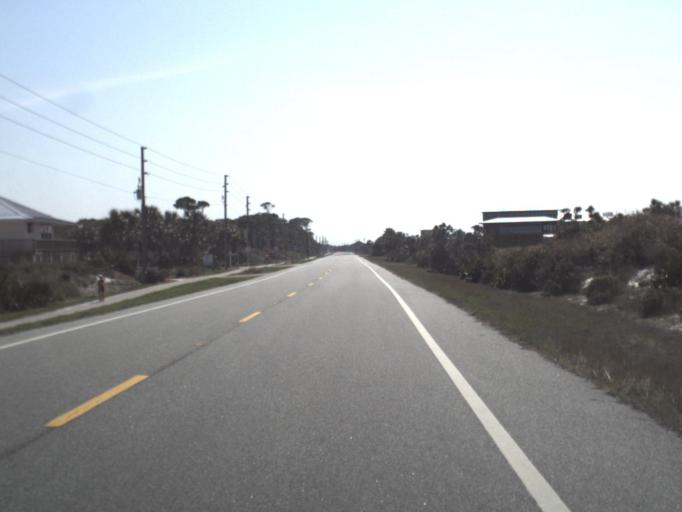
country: US
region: Florida
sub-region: Gulf County
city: Port Saint Joe
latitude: 29.7243
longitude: -85.3879
